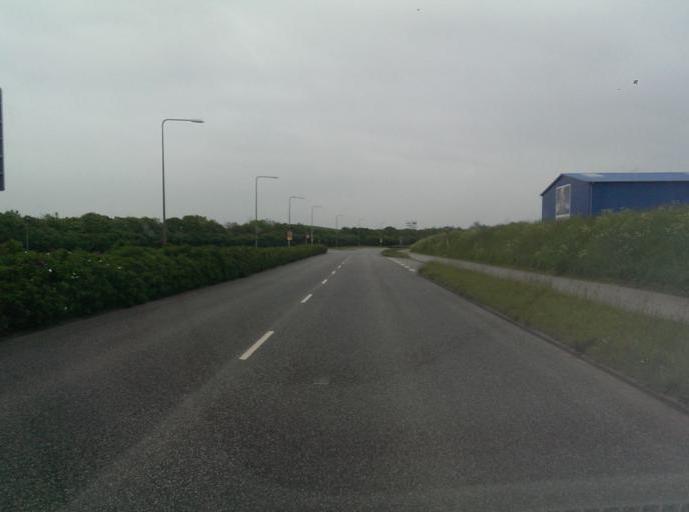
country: DK
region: South Denmark
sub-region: Esbjerg Kommune
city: Esbjerg
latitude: 55.4844
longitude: 8.4214
